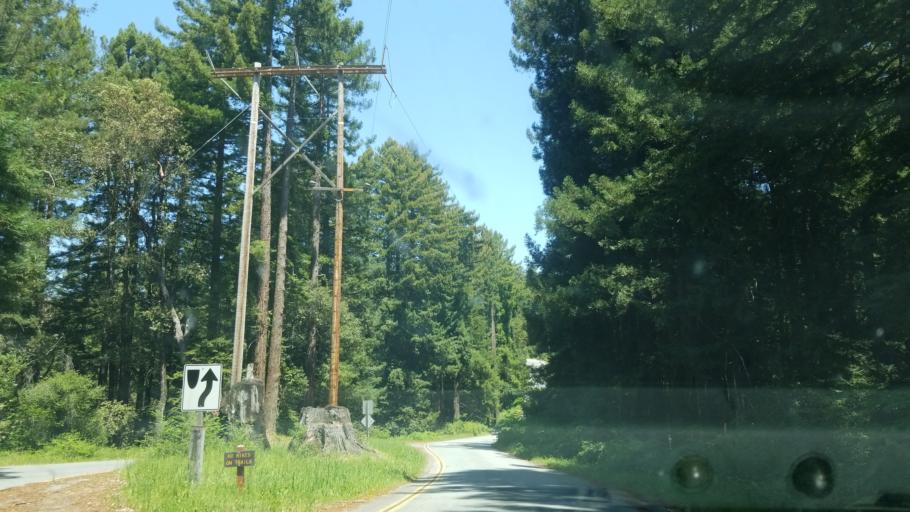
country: US
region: California
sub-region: Santa Cruz County
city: Interlaken
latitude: 36.9974
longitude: -121.7155
